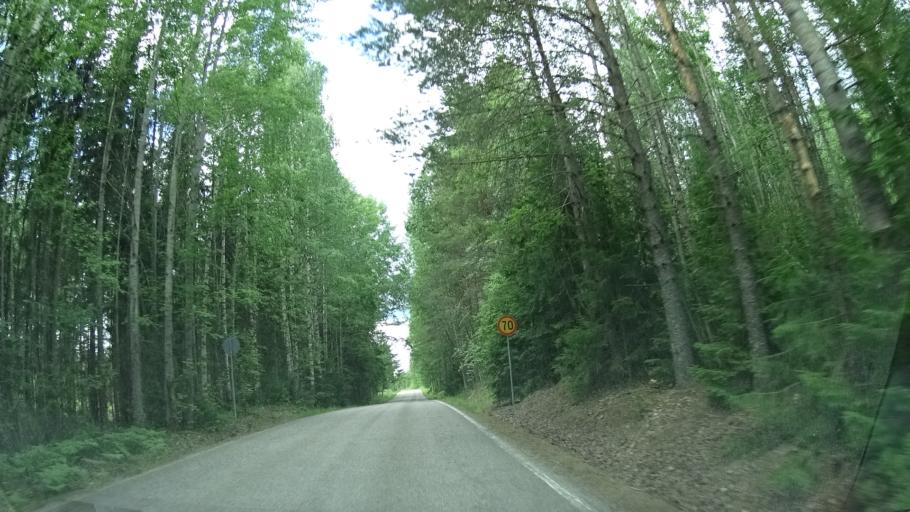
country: FI
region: Uusimaa
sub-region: Helsinki
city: Espoo
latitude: 60.4095
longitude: 24.5872
